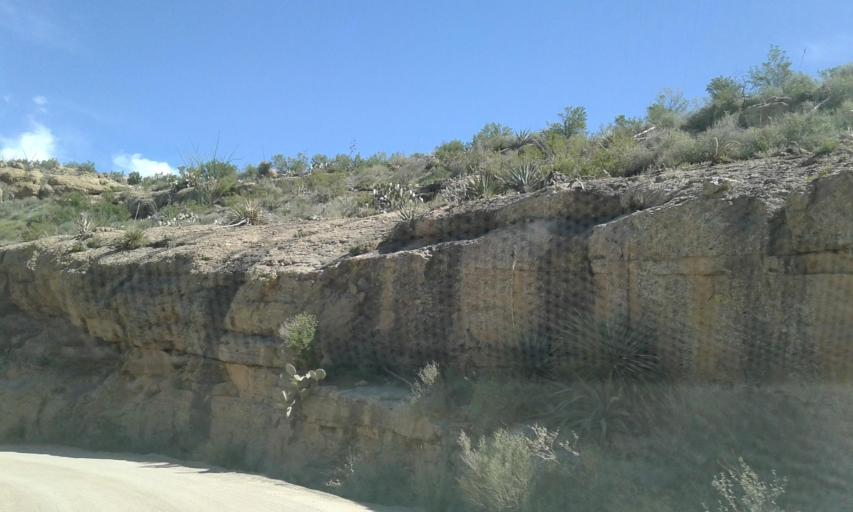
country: US
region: Arizona
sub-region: Pinal County
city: Gold Camp
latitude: 33.5327
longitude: -111.3107
